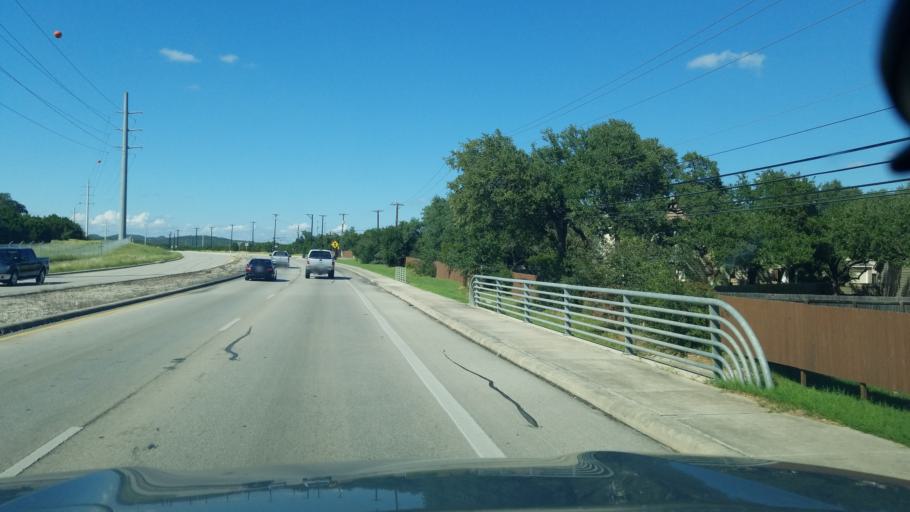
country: US
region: Texas
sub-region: Bexar County
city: Hollywood Park
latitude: 29.6485
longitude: -98.5184
